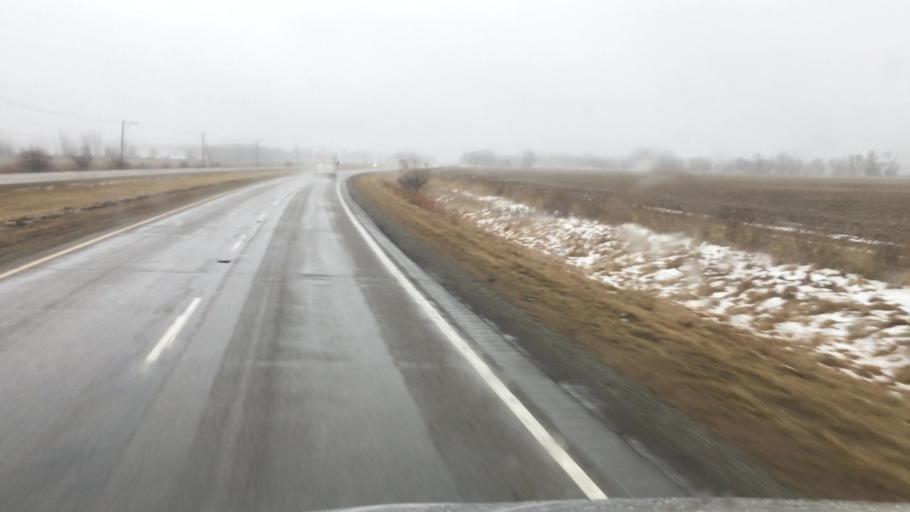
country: US
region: Indiana
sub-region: Newton County
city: Roselawn
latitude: 41.1213
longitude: -87.4493
